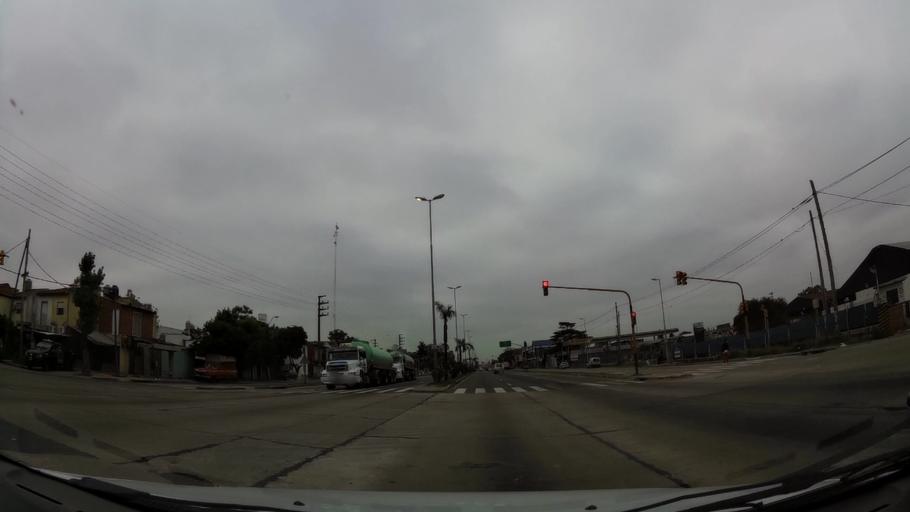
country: AR
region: Buenos Aires
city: San Justo
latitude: -34.6955
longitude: -58.5473
